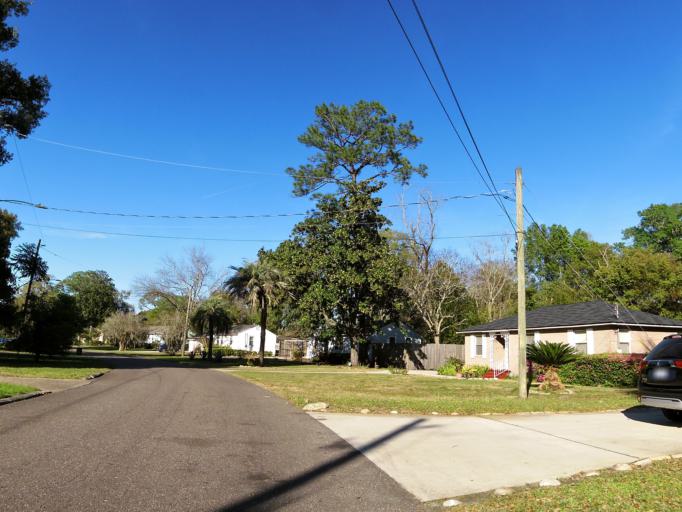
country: US
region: Florida
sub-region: Duval County
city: Jacksonville
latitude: 30.3964
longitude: -81.6774
